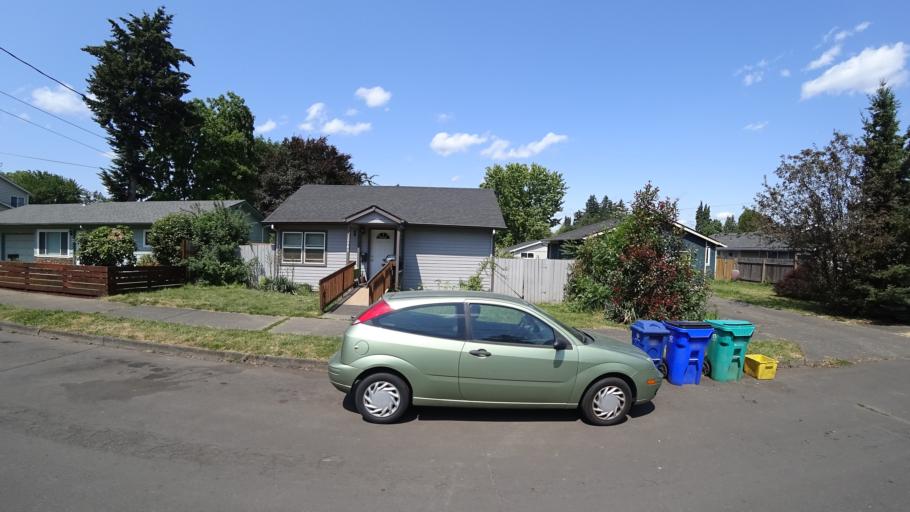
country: US
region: Oregon
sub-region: Washington County
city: West Haven
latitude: 45.5988
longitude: -122.7415
